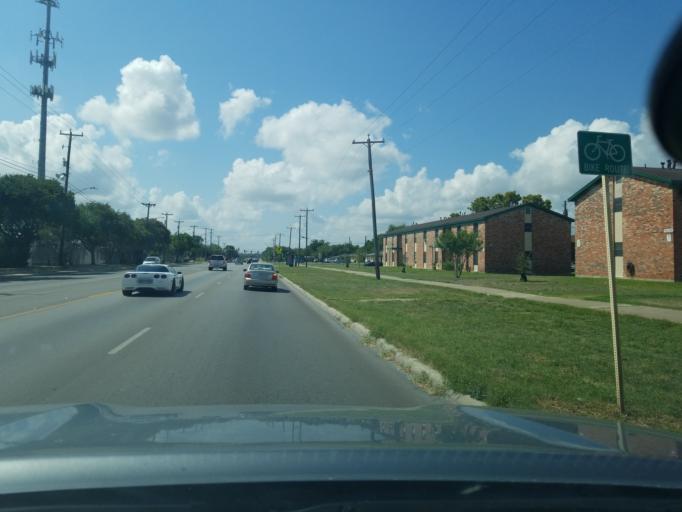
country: US
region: Texas
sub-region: Bexar County
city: San Antonio
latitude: 29.3482
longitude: -98.5342
